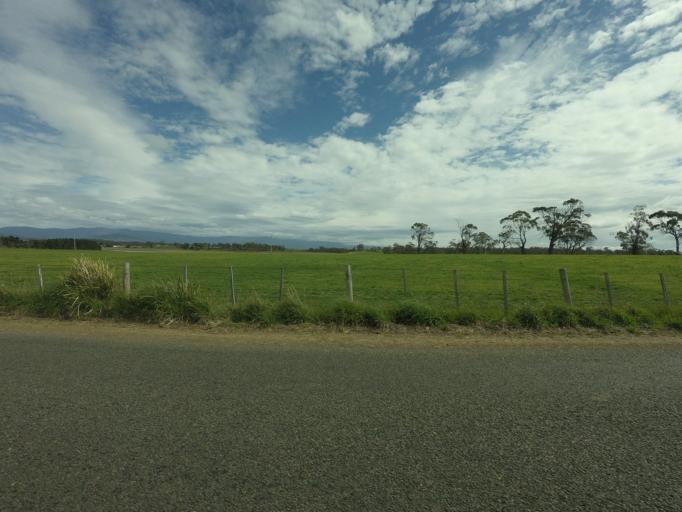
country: AU
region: Tasmania
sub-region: Northern Midlands
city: Longford
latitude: -41.7447
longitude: 147.2038
